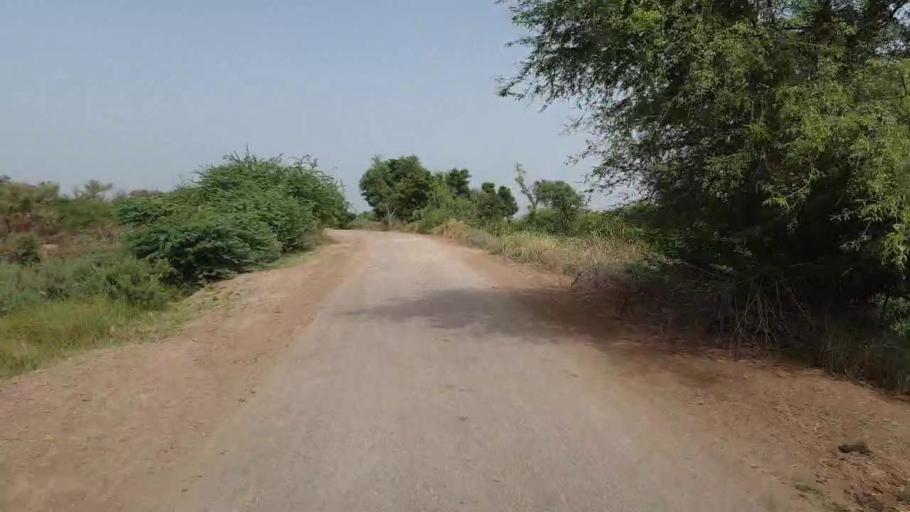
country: PK
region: Sindh
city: Daulatpur
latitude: 26.5463
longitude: 68.0669
